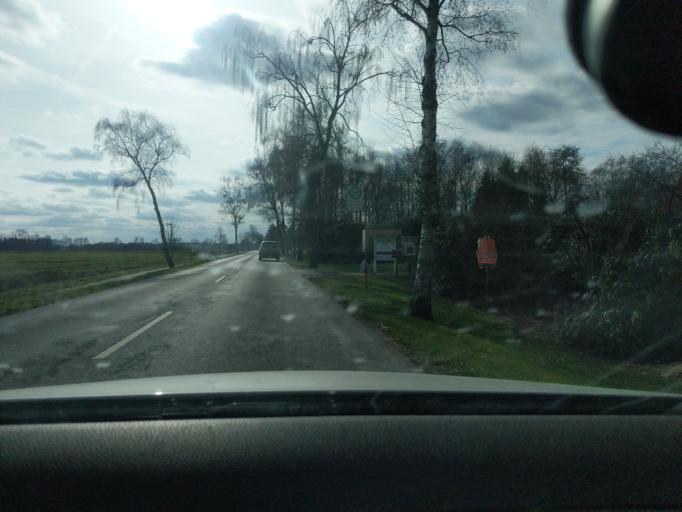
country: DE
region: Lower Saxony
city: Hammah
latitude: 53.6513
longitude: 9.3674
